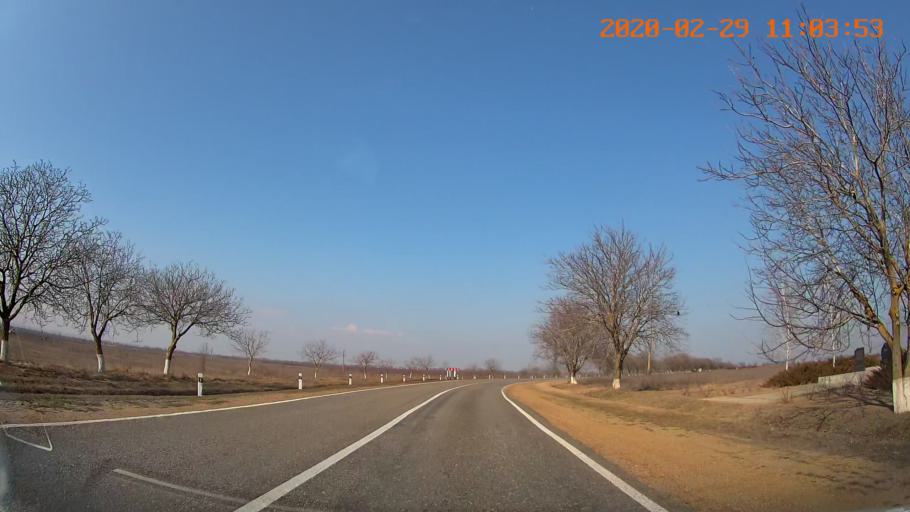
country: MD
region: Criuleni
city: Criuleni
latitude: 47.1824
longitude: 29.2092
